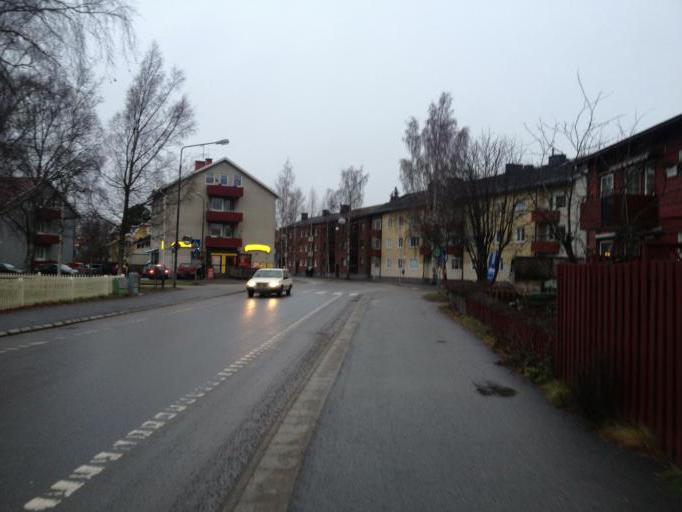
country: SE
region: Vaesterbotten
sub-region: Umea Kommun
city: Umea
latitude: 63.8218
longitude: 20.2852
